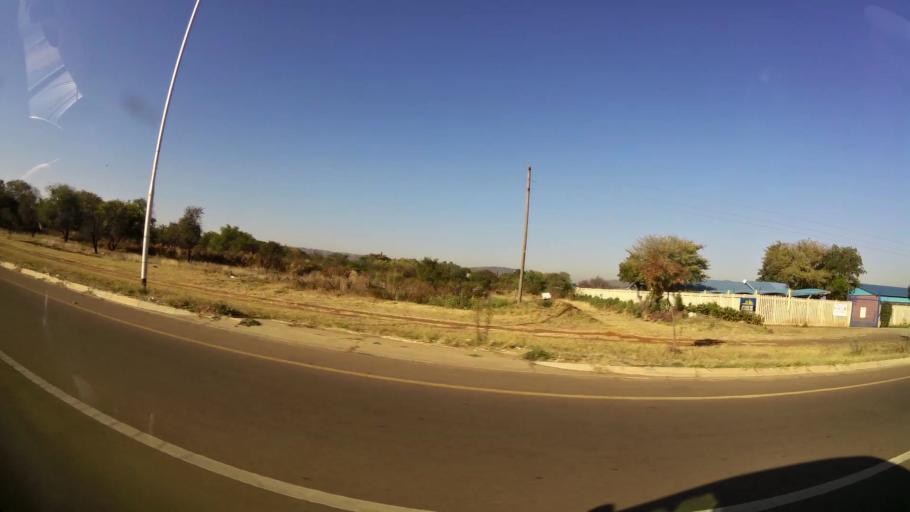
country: ZA
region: Gauteng
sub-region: City of Tshwane Metropolitan Municipality
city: Pretoria
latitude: -25.6542
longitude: 28.2001
